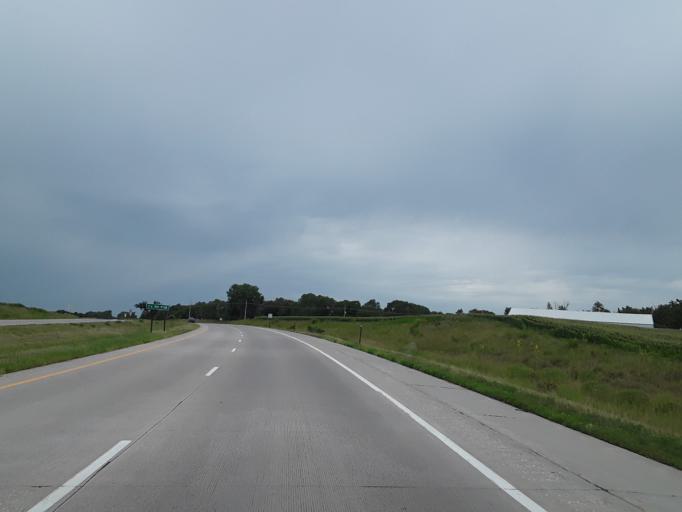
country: US
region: Nebraska
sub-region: Douglas County
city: Bennington
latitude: 41.4120
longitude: -96.0991
